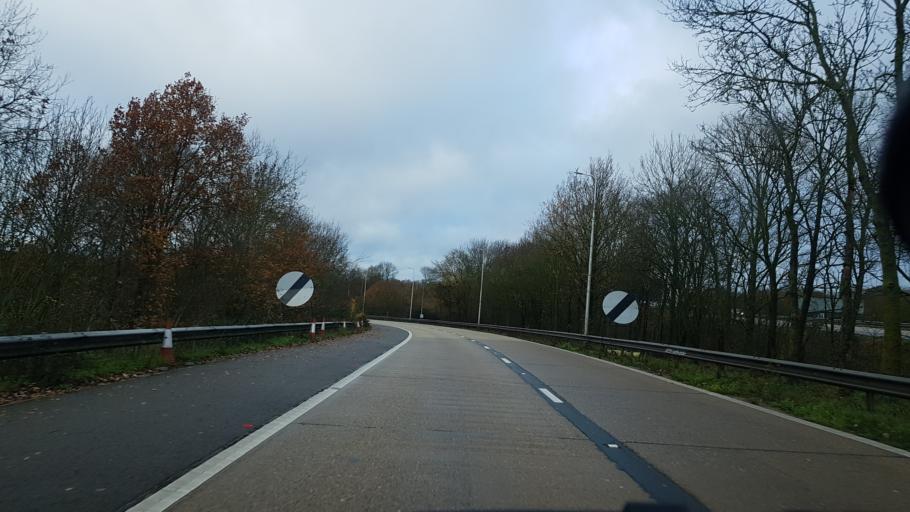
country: GB
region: England
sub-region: Wokingham
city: Wokingham
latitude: 51.4301
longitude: -0.8523
